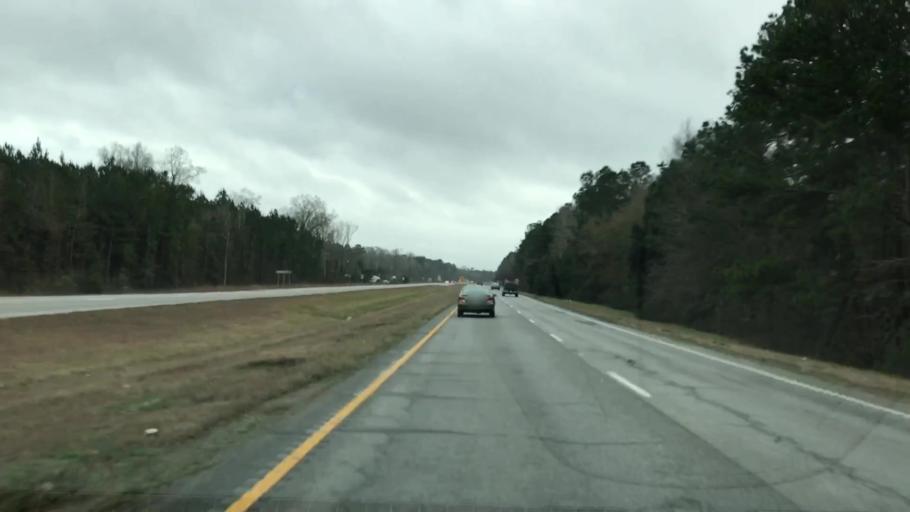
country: US
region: South Carolina
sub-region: Berkeley County
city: Moncks Corner
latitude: 33.1306
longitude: -80.0306
